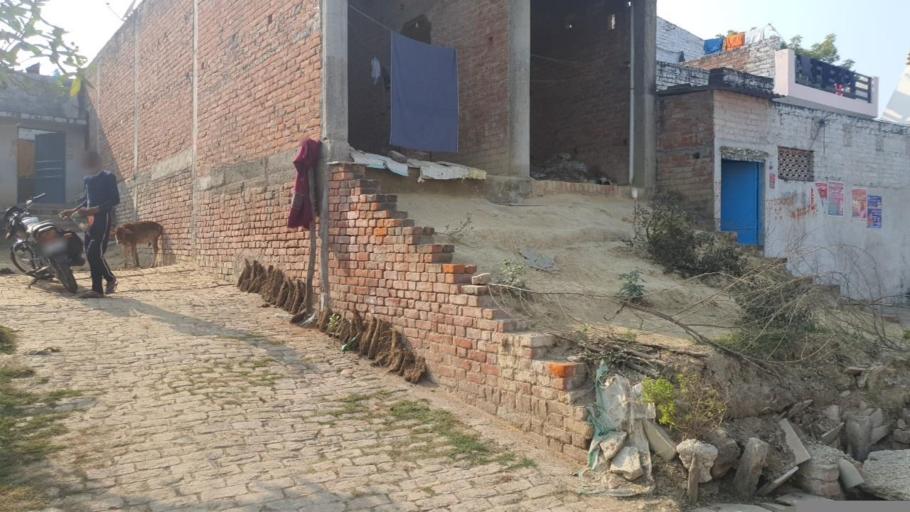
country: IN
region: Uttar Pradesh
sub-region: Lucknow District
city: Lucknow
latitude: 26.7960
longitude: 81.0092
